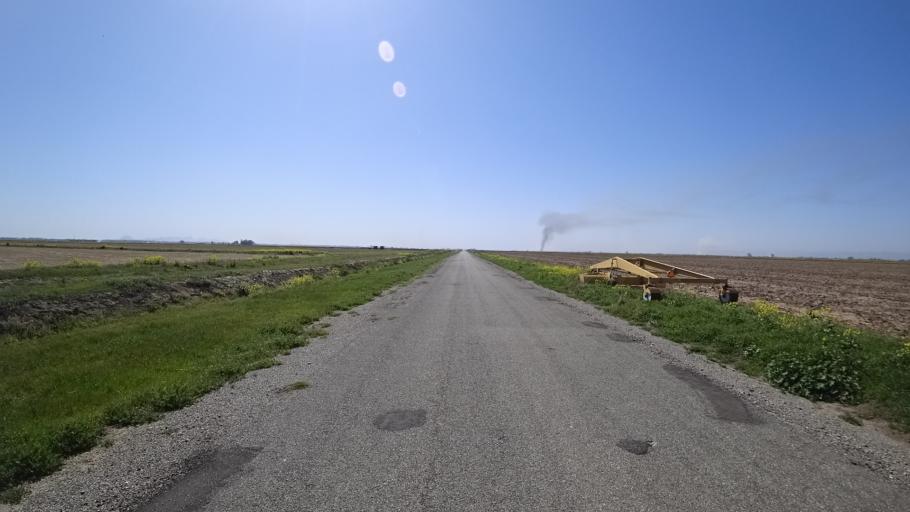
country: US
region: California
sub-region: Glenn County
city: Willows
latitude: 39.4392
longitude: -122.0646
